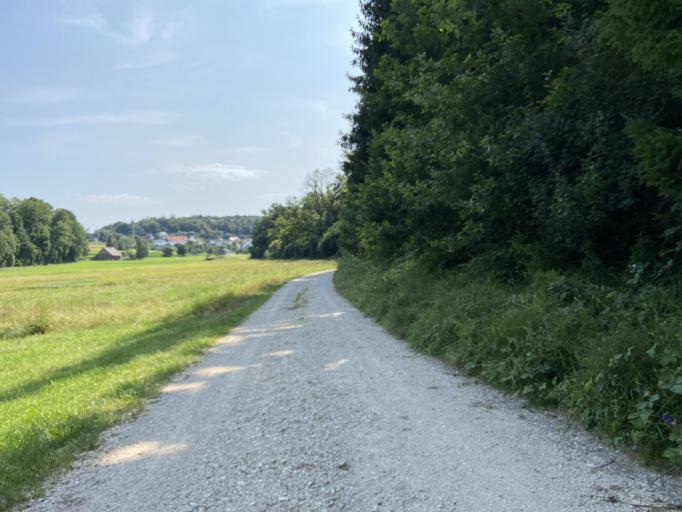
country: DE
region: Baden-Wuerttemberg
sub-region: Tuebingen Region
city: Bingen
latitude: 48.1133
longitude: 9.2921
